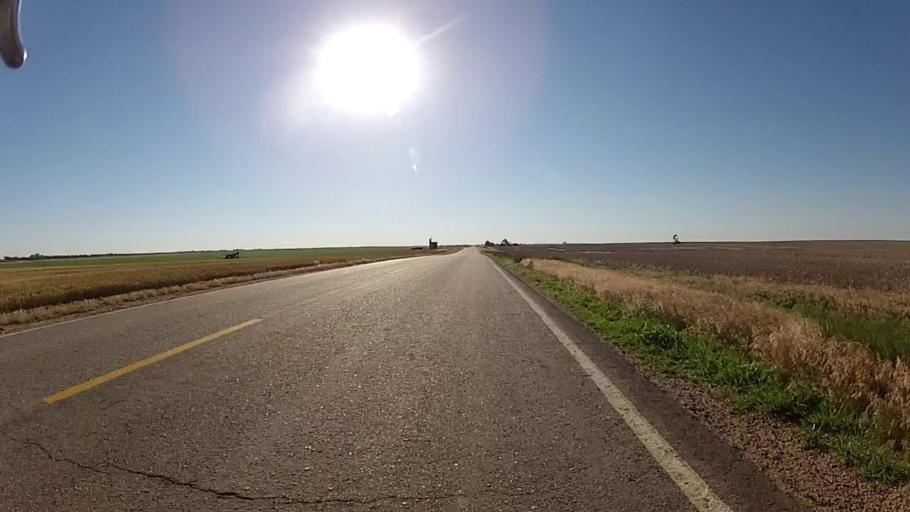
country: US
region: Kansas
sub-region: Ford County
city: Dodge City
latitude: 37.6461
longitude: -99.8240
